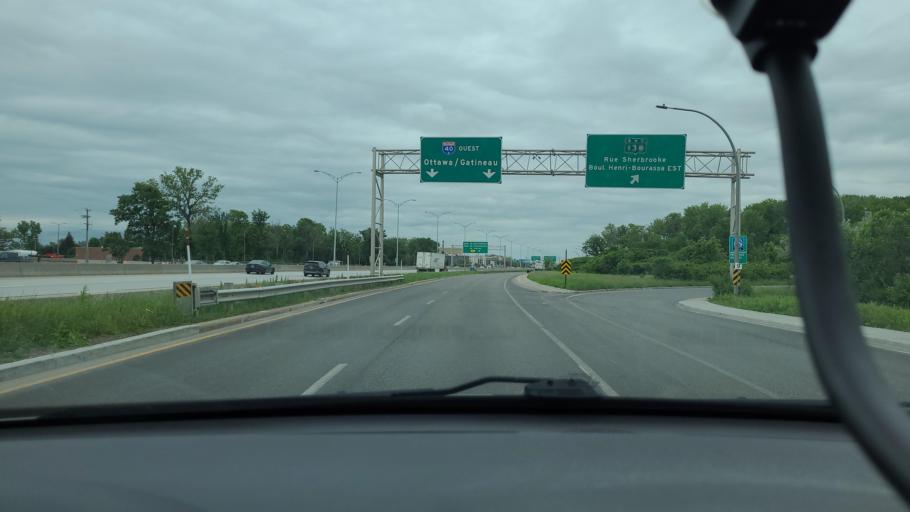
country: CA
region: Quebec
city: Montreal-Est
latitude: 45.6590
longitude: -73.5194
